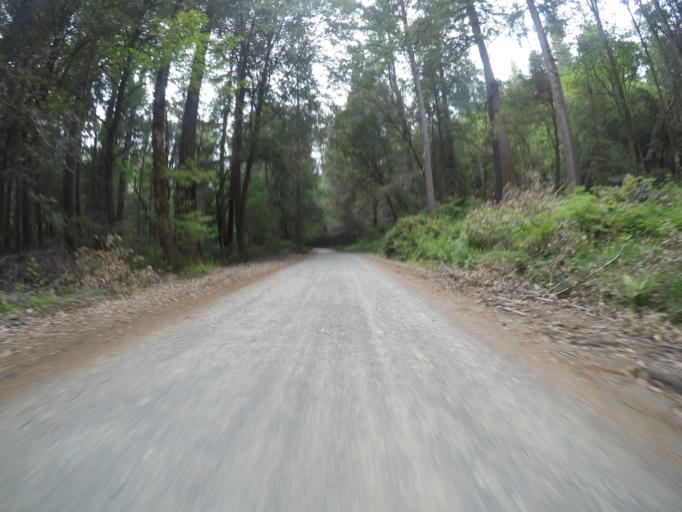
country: US
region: California
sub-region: Del Norte County
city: Bertsch-Oceanview
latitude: 41.6995
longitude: -123.8987
